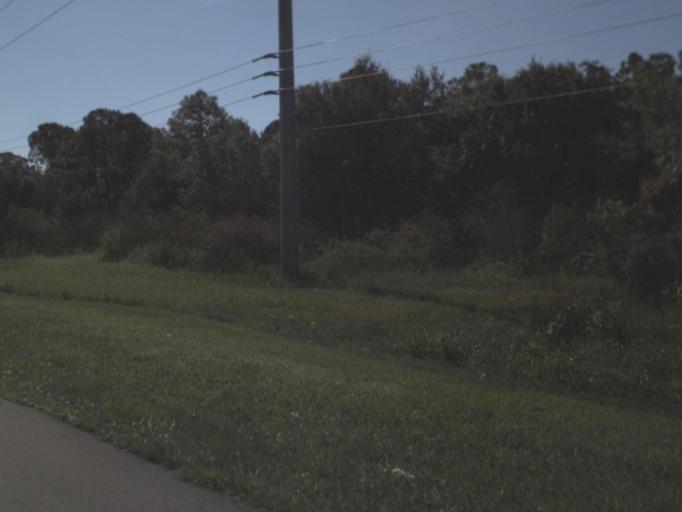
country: US
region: Florida
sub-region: Lee County
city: Gateway
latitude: 26.5895
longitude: -81.7315
